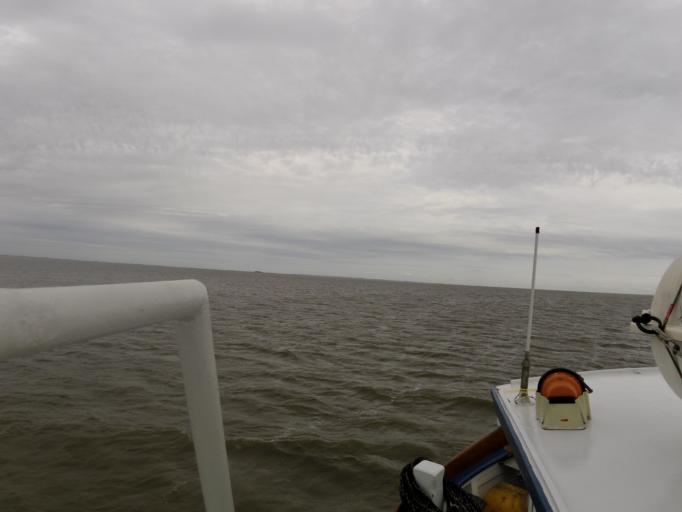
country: DE
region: Schleswig-Holstein
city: Langeness
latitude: 54.6136
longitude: 8.6276
